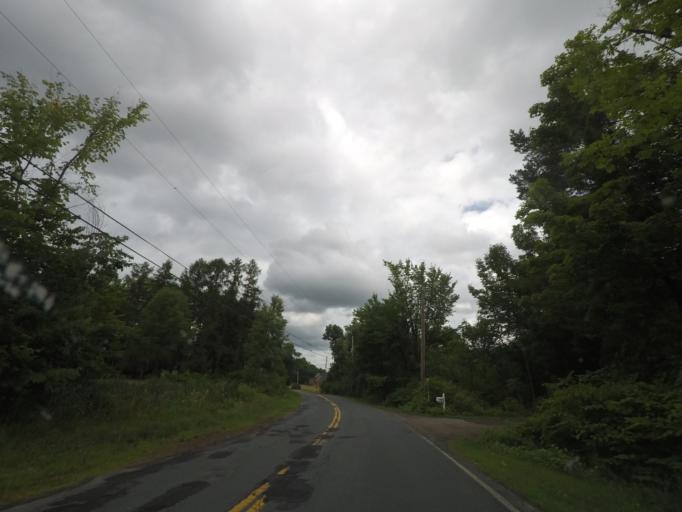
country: US
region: New York
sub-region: Rensselaer County
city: Wynantskill
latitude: 42.6786
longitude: -73.6349
